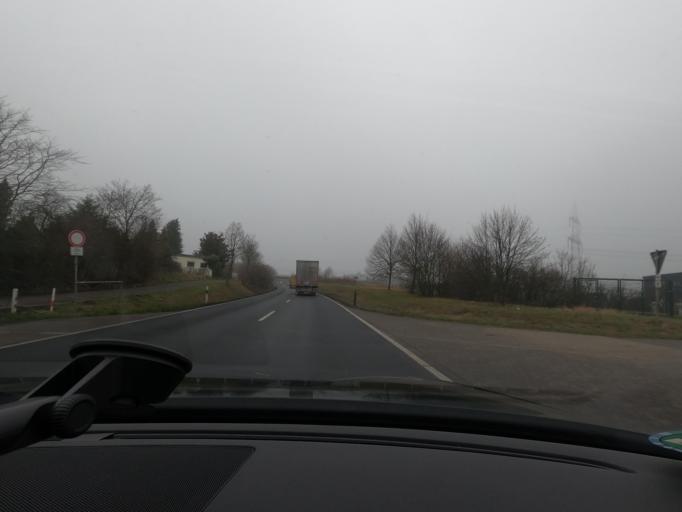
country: DE
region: North Rhine-Westphalia
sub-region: Regierungsbezirk Koln
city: Merzenich
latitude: 50.8365
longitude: 6.5278
